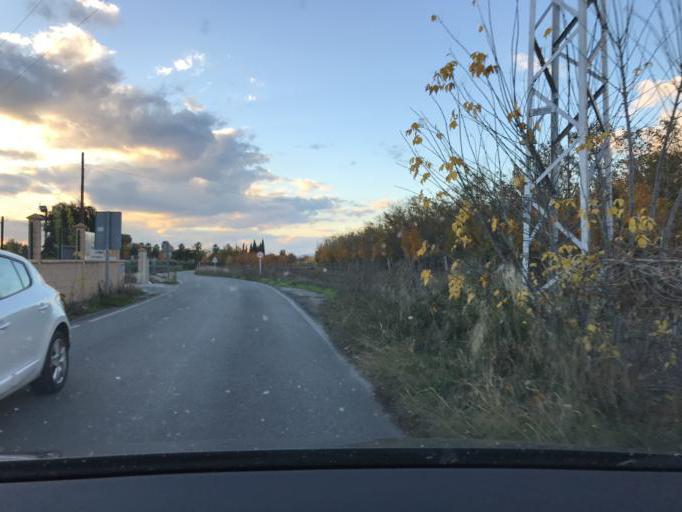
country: ES
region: Andalusia
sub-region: Provincia de Granada
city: Armilla
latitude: 37.1668
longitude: -3.6247
